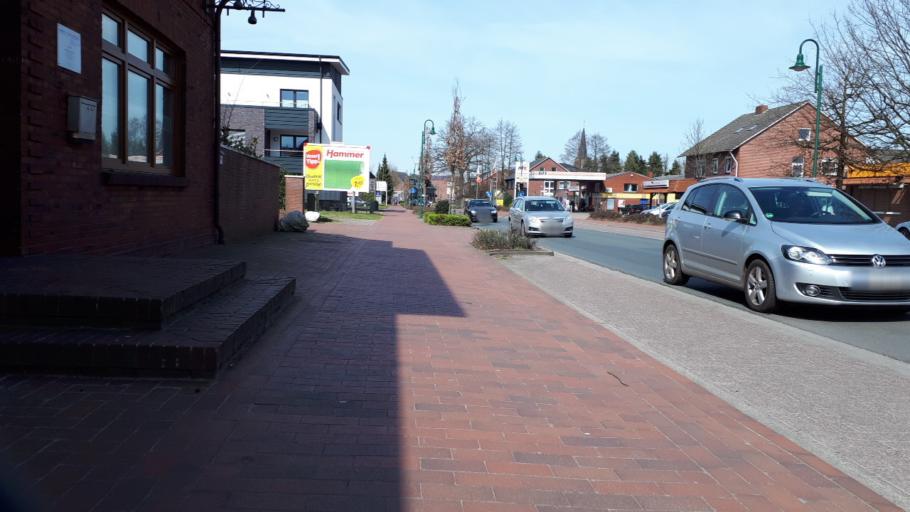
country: DE
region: Lower Saxony
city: Garrel
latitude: 52.9522
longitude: 8.0269
